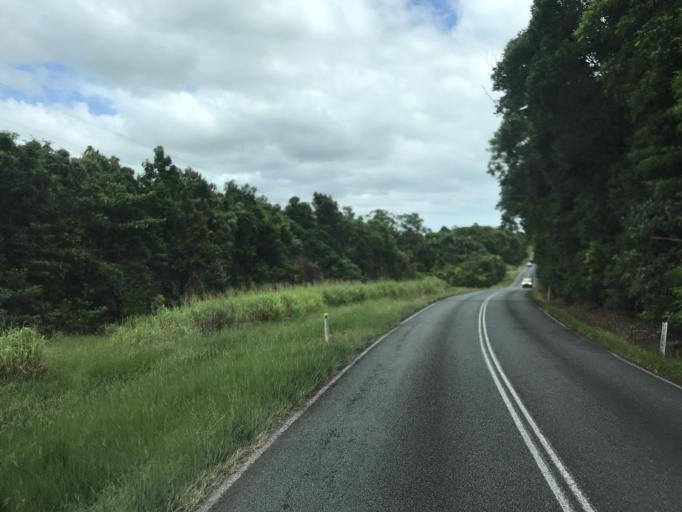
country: AU
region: Queensland
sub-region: Cassowary Coast
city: Innisfail
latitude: -17.8365
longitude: 146.0522
